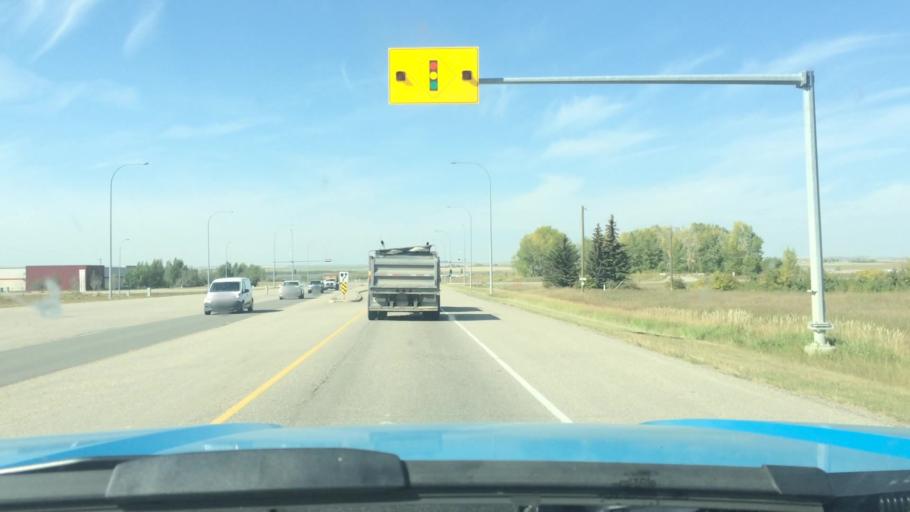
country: CA
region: Alberta
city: Airdrie
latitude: 51.2126
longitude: -113.9786
